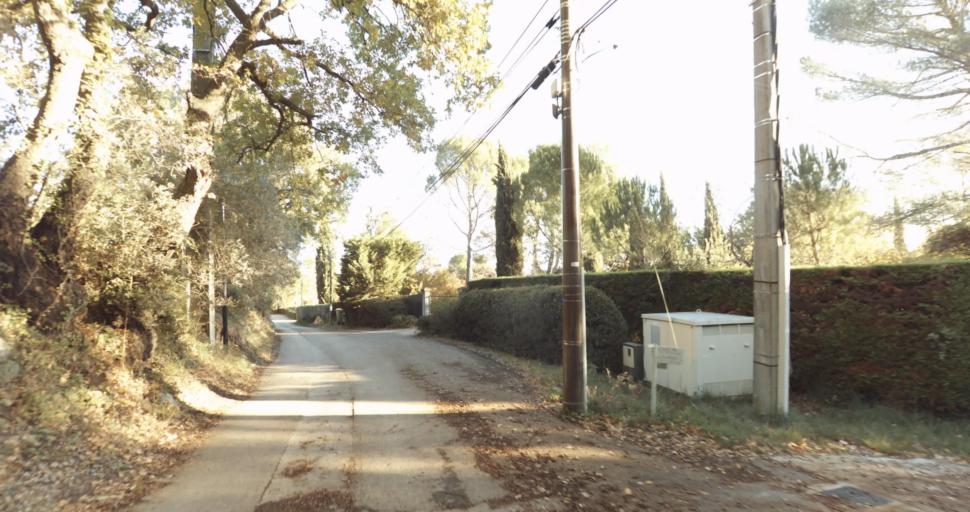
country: FR
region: Provence-Alpes-Cote d'Azur
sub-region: Departement des Bouches-du-Rhone
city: Venelles
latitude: 43.6061
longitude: 5.4816
